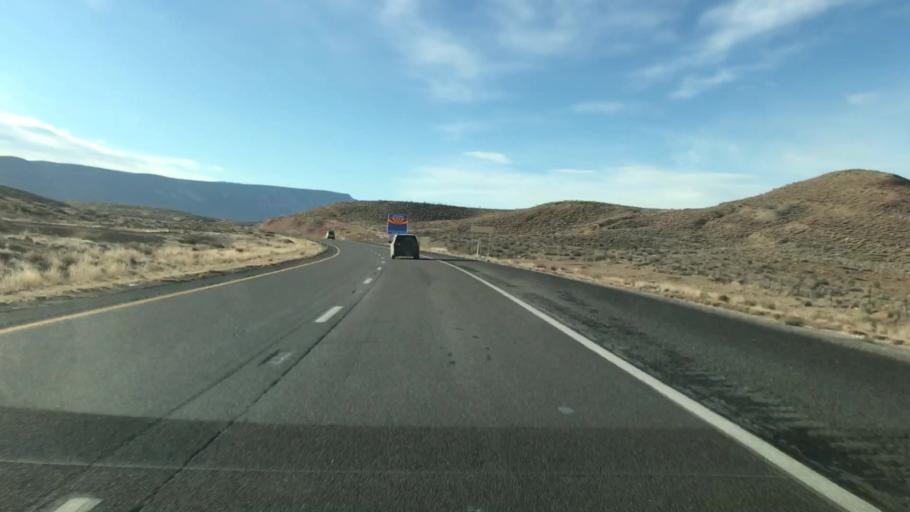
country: US
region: Utah
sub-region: Washington County
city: Saint George
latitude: 36.9998
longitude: -113.6245
